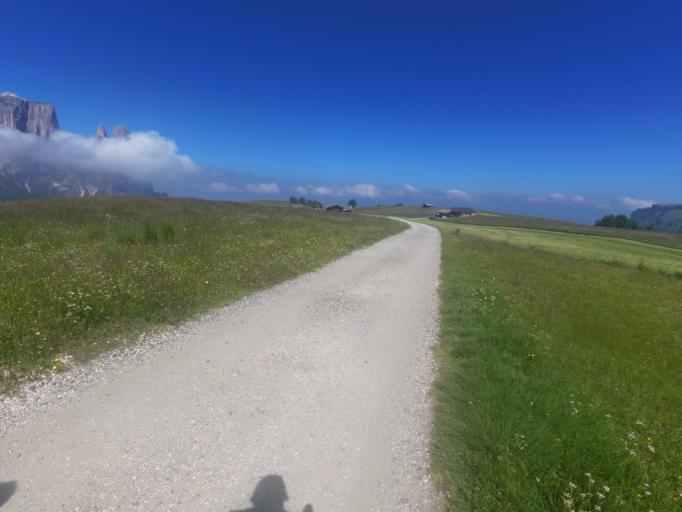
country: IT
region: Trentino-Alto Adige
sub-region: Bolzano
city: Siusi
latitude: 46.5271
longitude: 11.6082
